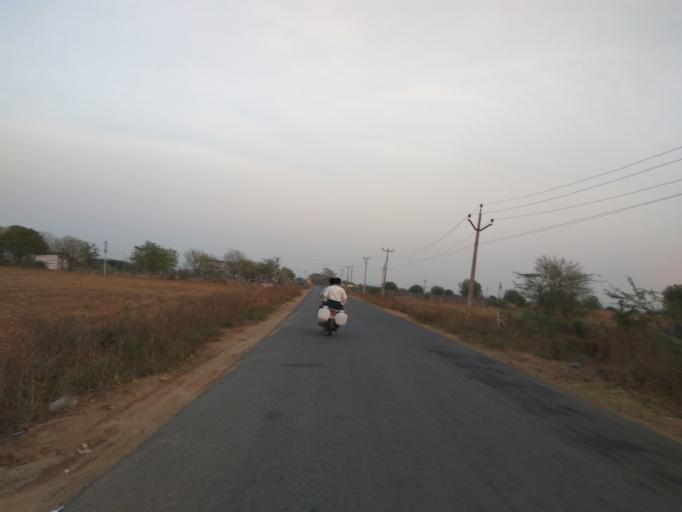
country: IN
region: Andhra Pradesh
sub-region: Prakasam
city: Markapur
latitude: 15.7531
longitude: 79.2267
